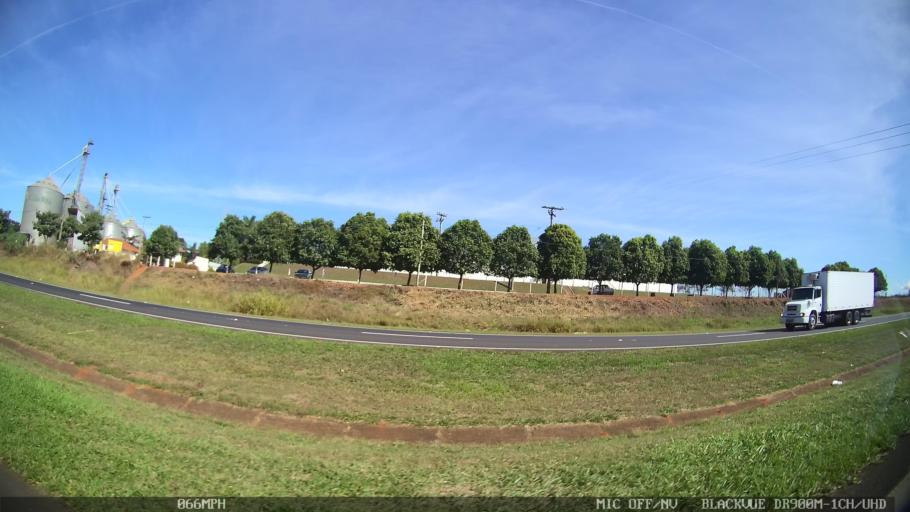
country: BR
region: Sao Paulo
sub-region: Pirassununga
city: Pirassununga
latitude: -22.0223
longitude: -47.4377
